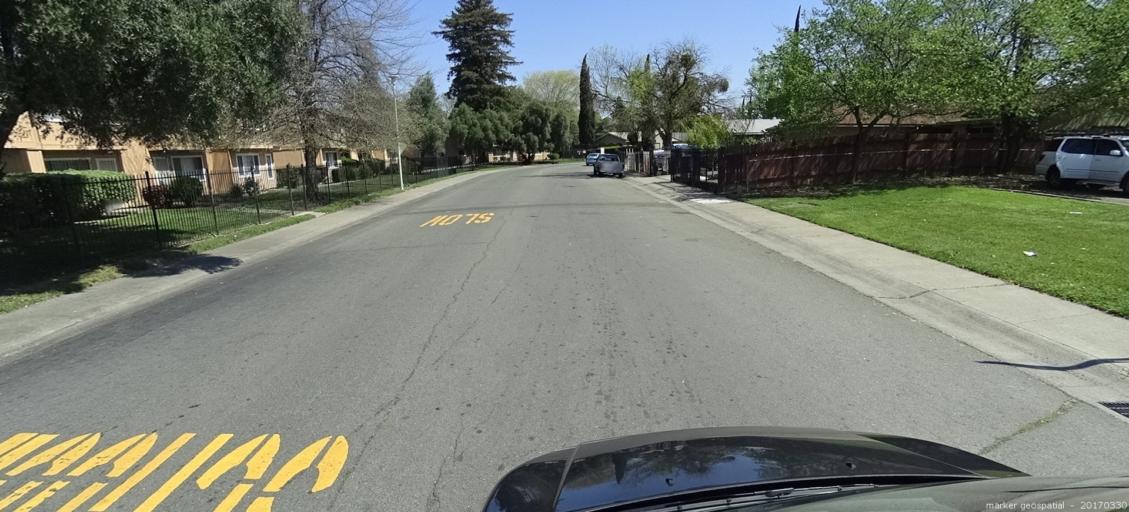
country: US
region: California
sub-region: Sacramento County
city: Florin
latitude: 38.4711
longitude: -121.4322
